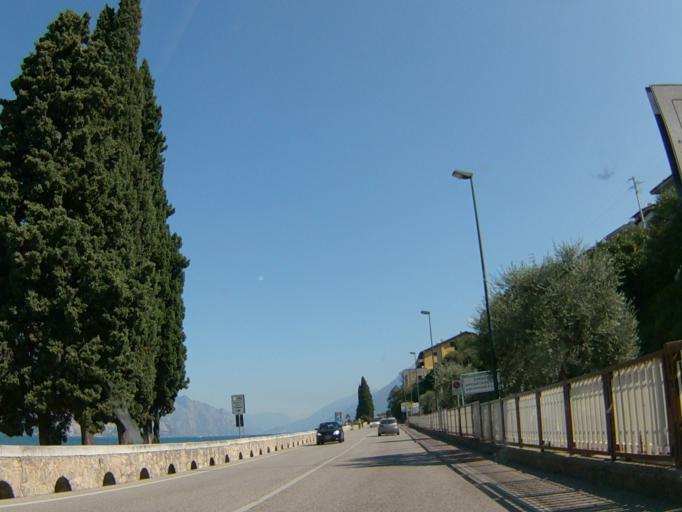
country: IT
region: Veneto
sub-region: Provincia di Verona
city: San Zeno di Montagna
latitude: 45.6684
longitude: 10.7330
